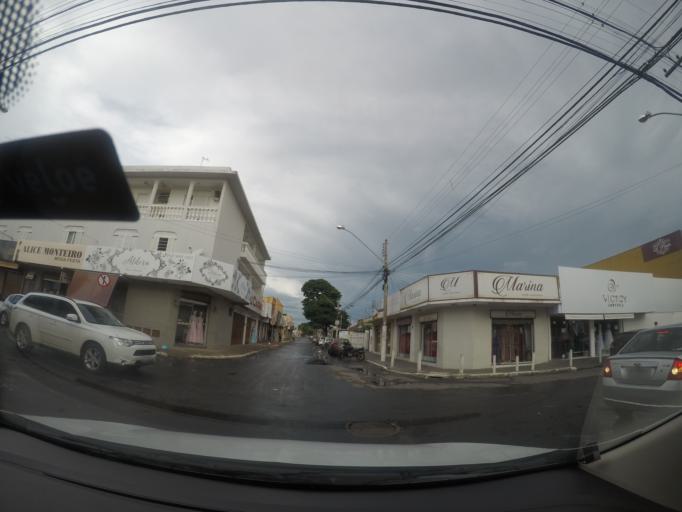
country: BR
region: Goias
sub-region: Goiania
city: Goiania
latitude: -16.6673
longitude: -49.2916
